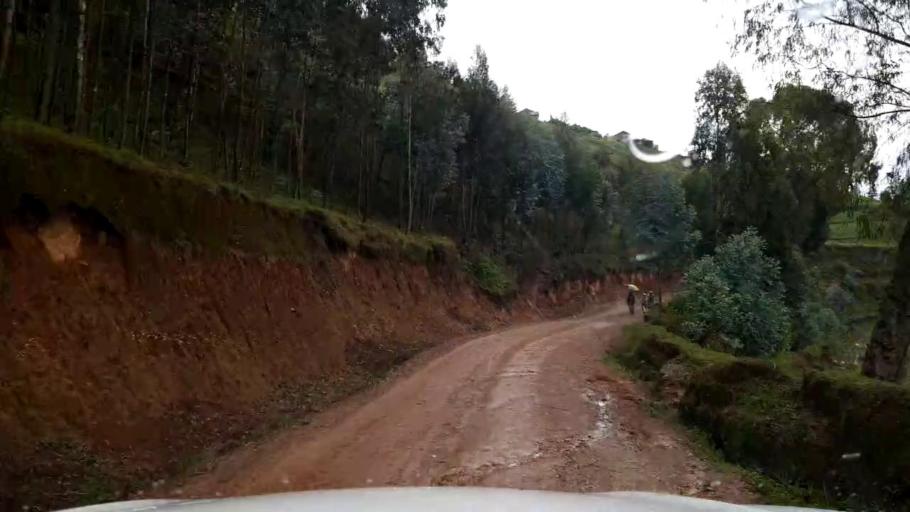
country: RW
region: Western Province
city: Kibuye
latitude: -2.0196
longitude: 29.4621
